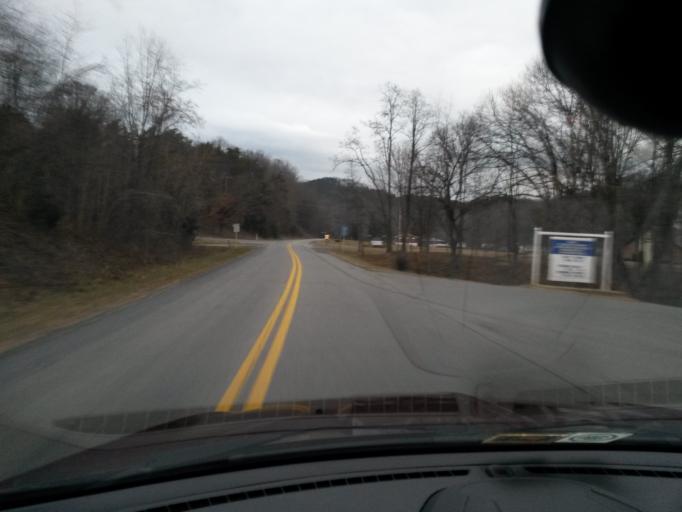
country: US
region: Virginia
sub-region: Alleghany County
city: Clifton Forge
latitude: 37.8302
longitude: -79.7913
